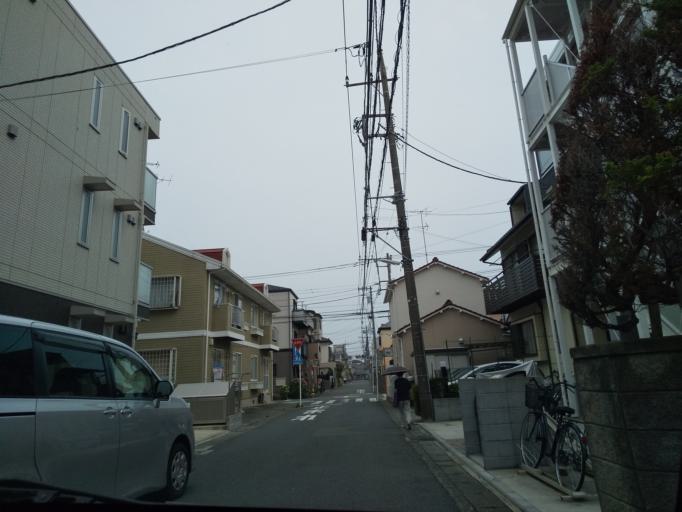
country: JP
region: Kanagawa
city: Minami-rinkan
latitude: 35.4684
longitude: 139.4248
